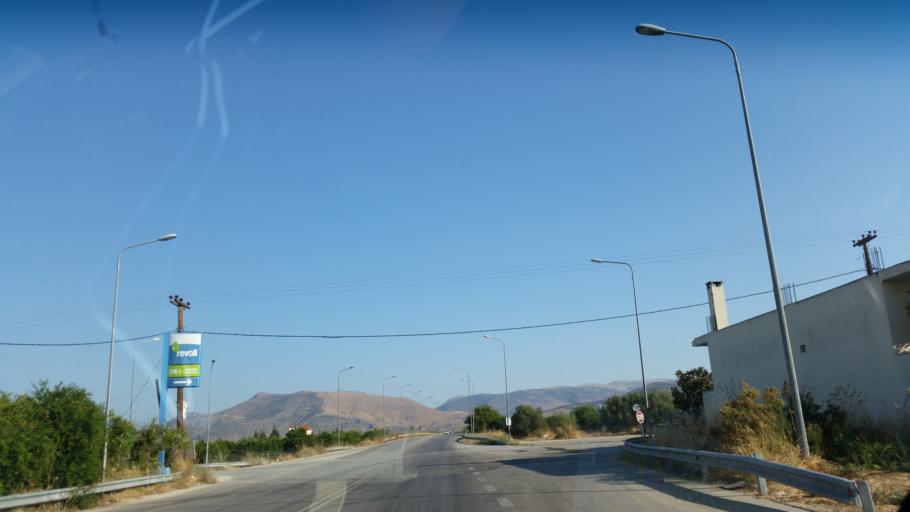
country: GR
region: Peloponnese
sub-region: Nomos Argolidos
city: Ayia Trias
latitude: 37.6329
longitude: 22.8173
